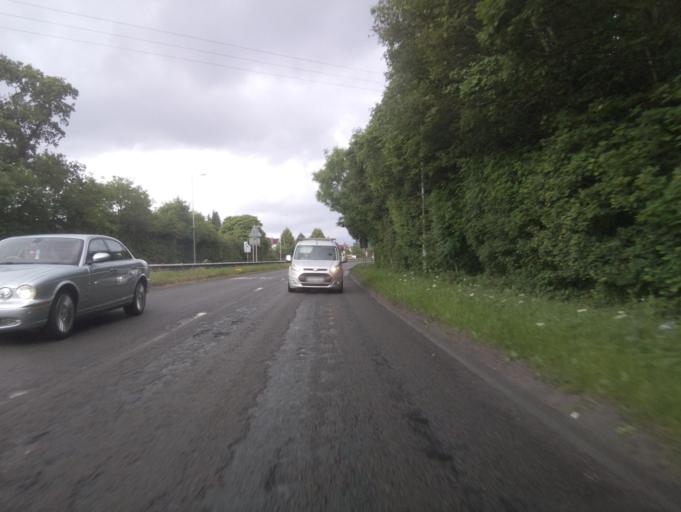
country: GB
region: England
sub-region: Dudley
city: Kingswinford
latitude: 52.5438
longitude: -2.1746
